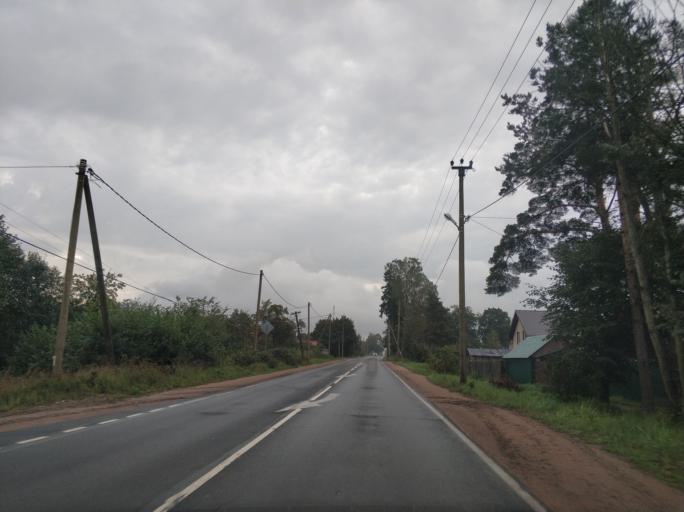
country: RU
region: Leningrad
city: Borisova Griva
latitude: 60.0848
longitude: 30.8886
